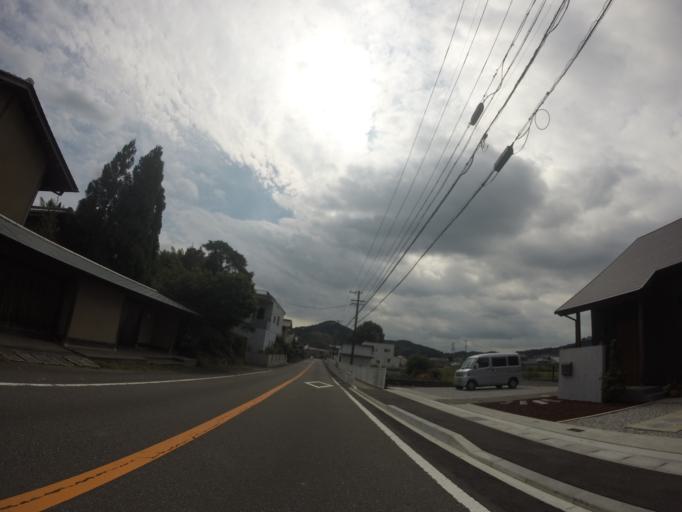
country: JP
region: Shizuoka
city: Shimada
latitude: 34.8584
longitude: 138.1802
